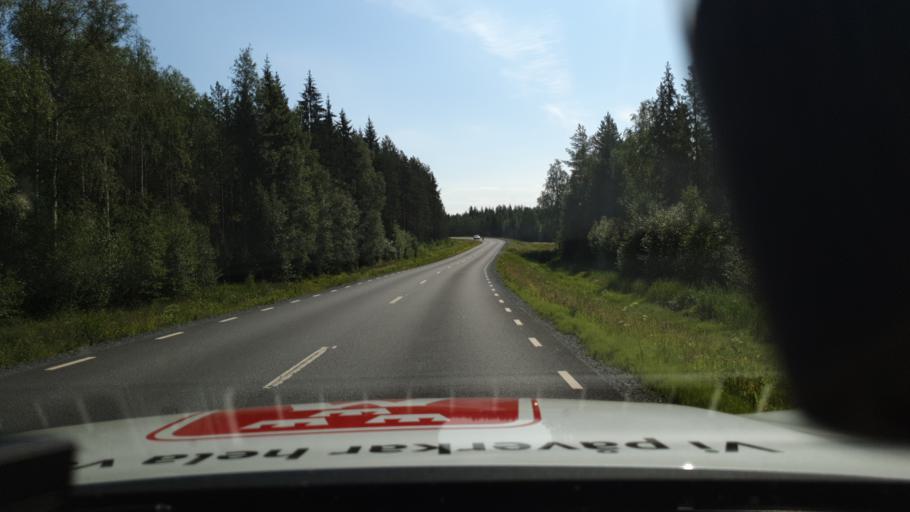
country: SE
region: Norrbotten
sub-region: Bodens Kommun
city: Saevast
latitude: 65.8389
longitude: 21.8261
